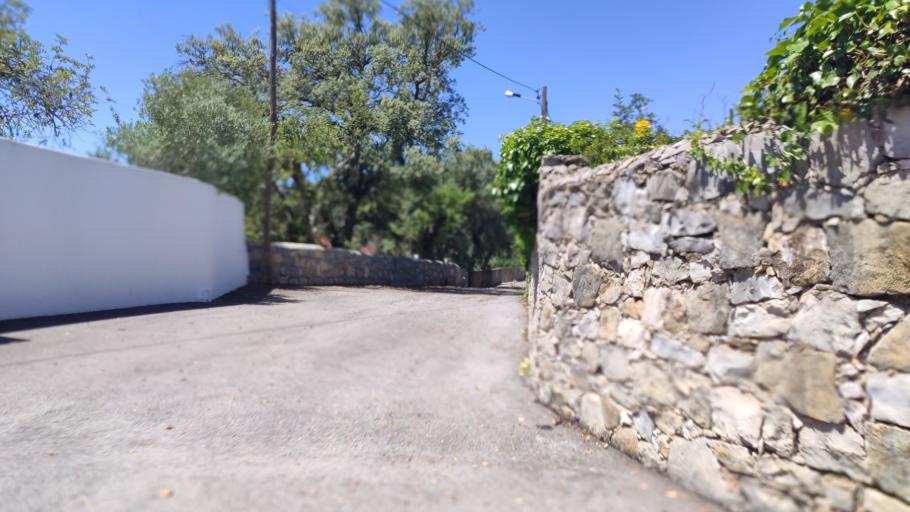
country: PT
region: Faro
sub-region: Sao Bras de Alportel
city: Sao Bras de Alportel
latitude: 37.1709
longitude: -7.9047
